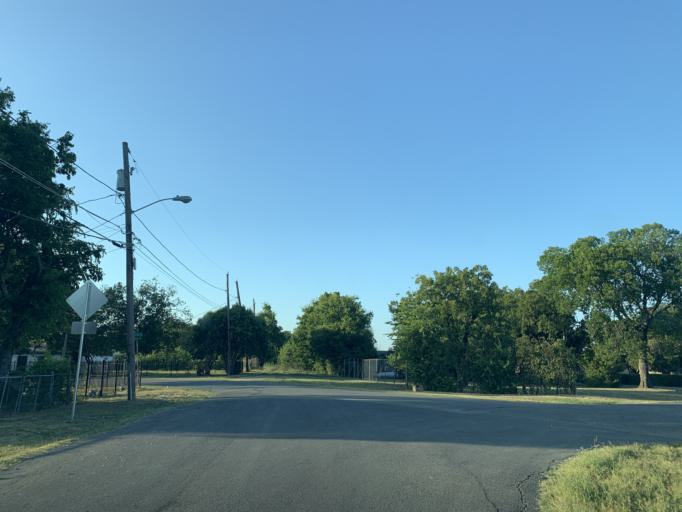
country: US
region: Texas
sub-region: Dallas County
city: Dallas
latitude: 32.7025
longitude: -96.8088
